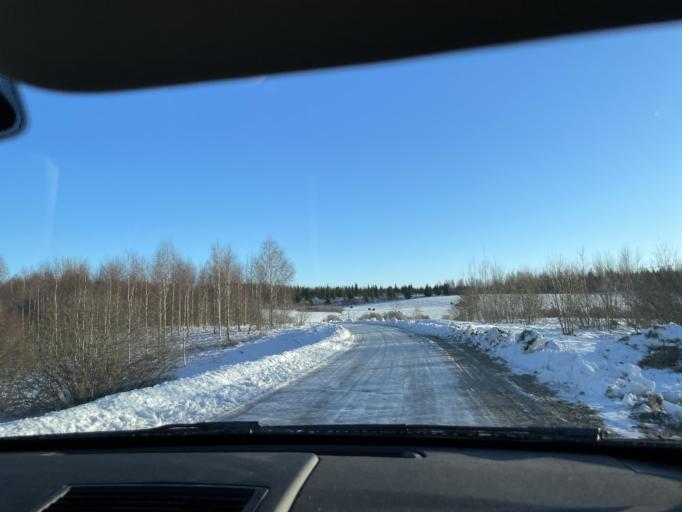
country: LV
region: Ludzas Rajons
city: Ludza
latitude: 56.4602
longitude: 27.6114
